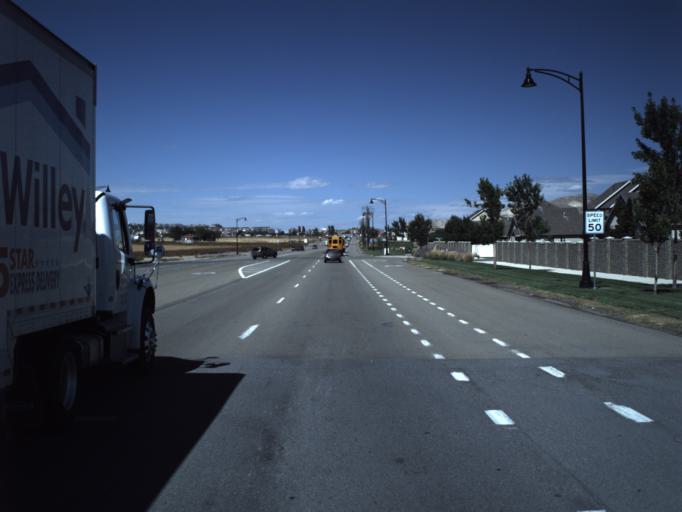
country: US
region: Utah
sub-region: Utah County
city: Saratoga Springs
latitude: 40.3744
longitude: -111.9163
